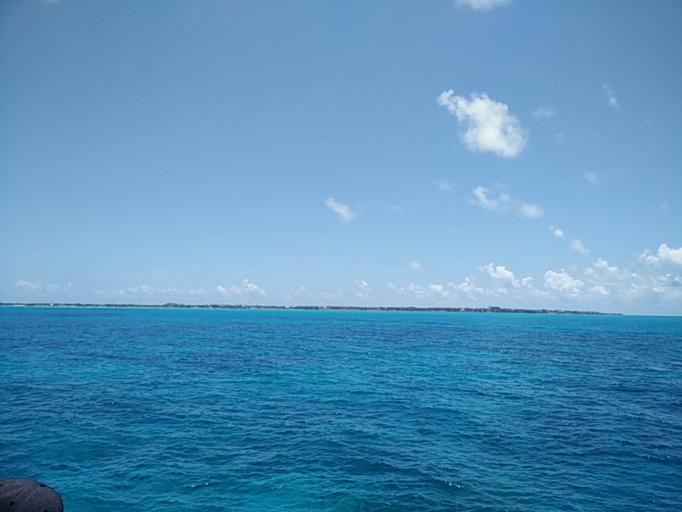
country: MX
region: Quintana Roo
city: Isla Mujeres
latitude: 21.2072
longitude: -86.7593
